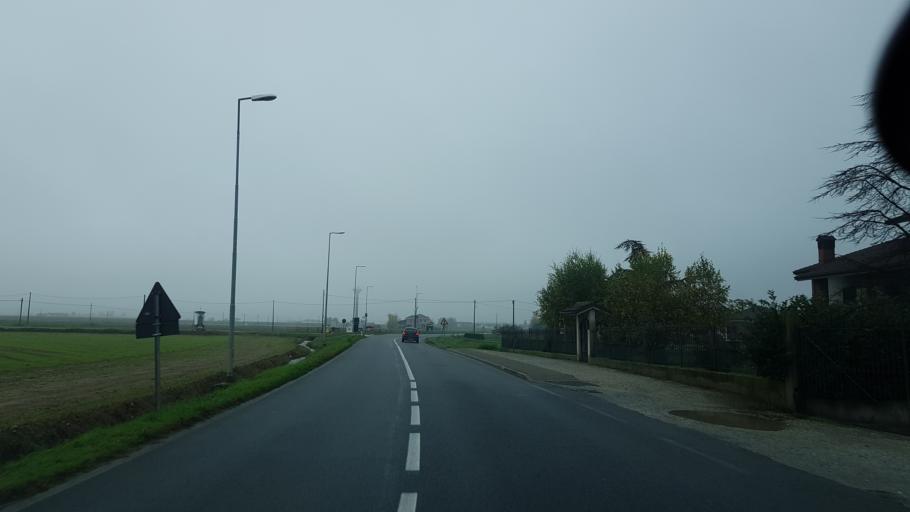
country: IT
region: Piedmont
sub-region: Provincia di Cuneo
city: Vottignasco
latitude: 44.5621
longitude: 7.5746
